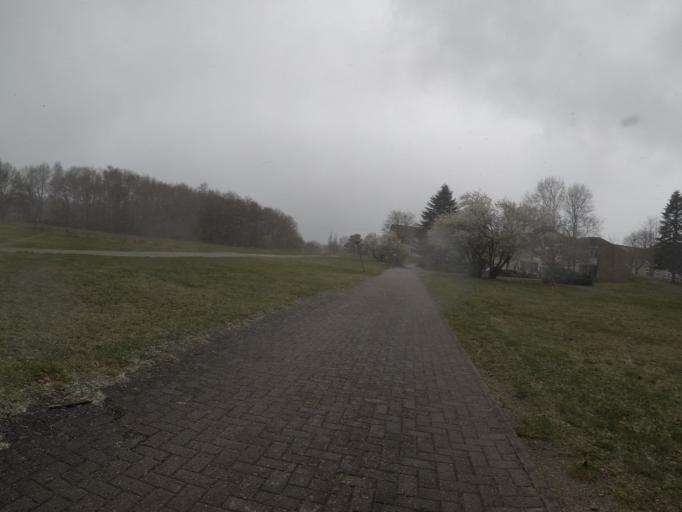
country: DE
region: Lower Saxony
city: Langen
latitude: 53.6149
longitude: 8.6338
